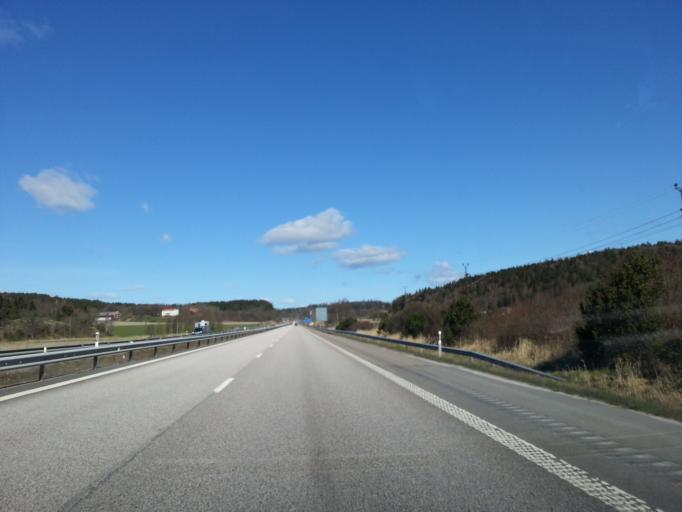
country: SE
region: Vaestra Goetaland
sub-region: Uddevalla Kommun
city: Ljungskile
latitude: 58.2769
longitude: 11.8857
